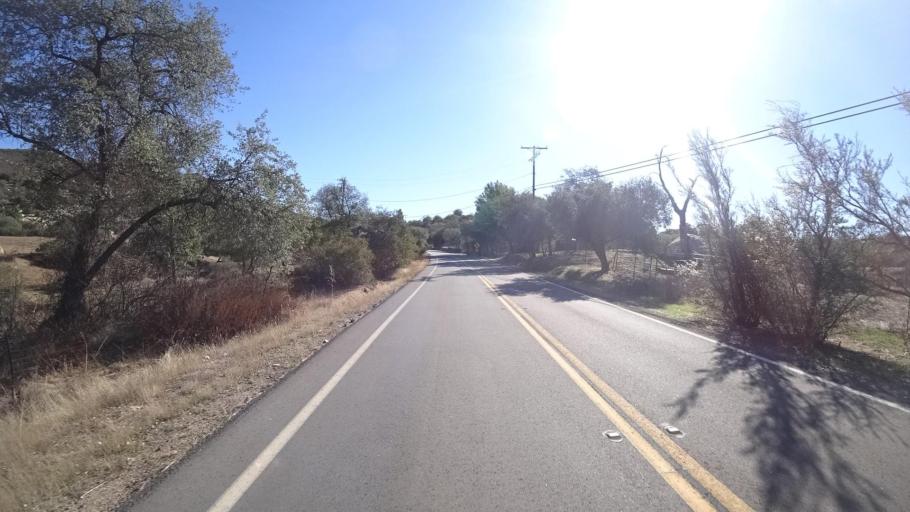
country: MX
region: Baja California
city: Tecate
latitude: 32.6763
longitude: -116.7215
